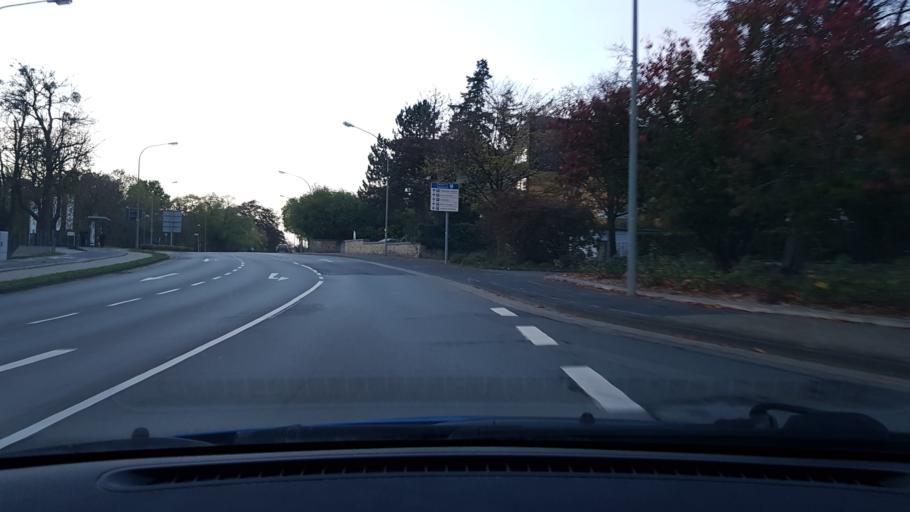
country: DE
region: Lower Saxony
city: Helmstedt
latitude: 52.2281
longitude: 11.0177
